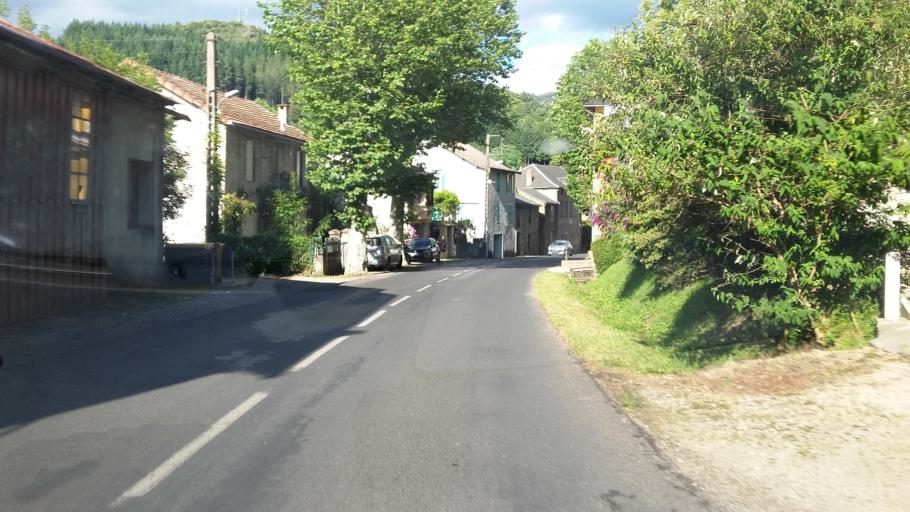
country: FR
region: Languedoc-Roussillon
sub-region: Departement de la Lozere
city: Meyrueis
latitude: 44.0245
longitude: 3.3558
